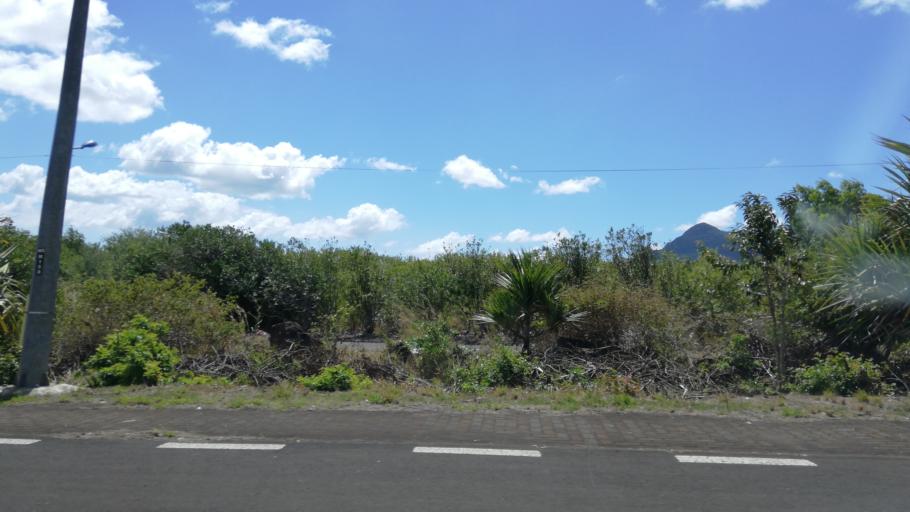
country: MU
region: Plaines Wilhems
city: Ebene
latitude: -20.2391
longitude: 57.4815
